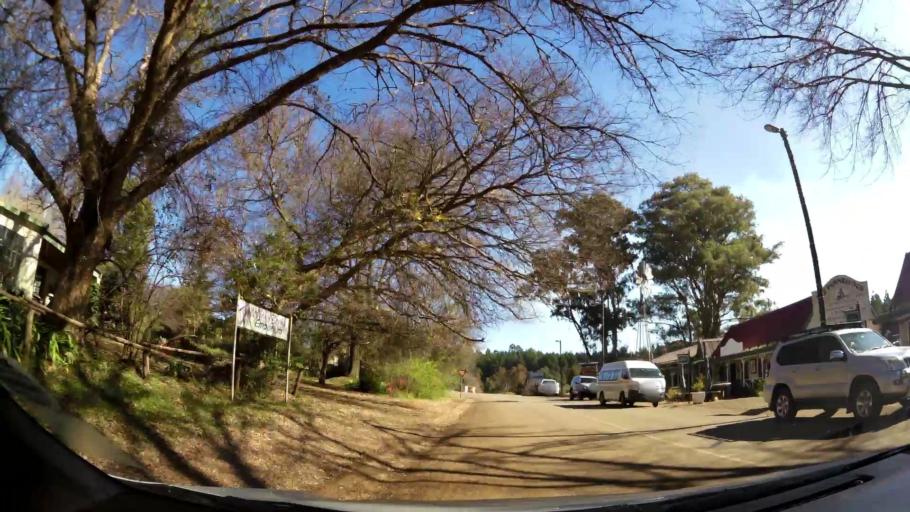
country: ZA
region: Limpopo
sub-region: Capricorn District Municipality
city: Mankoeng
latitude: -23.9430
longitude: 29.9391
